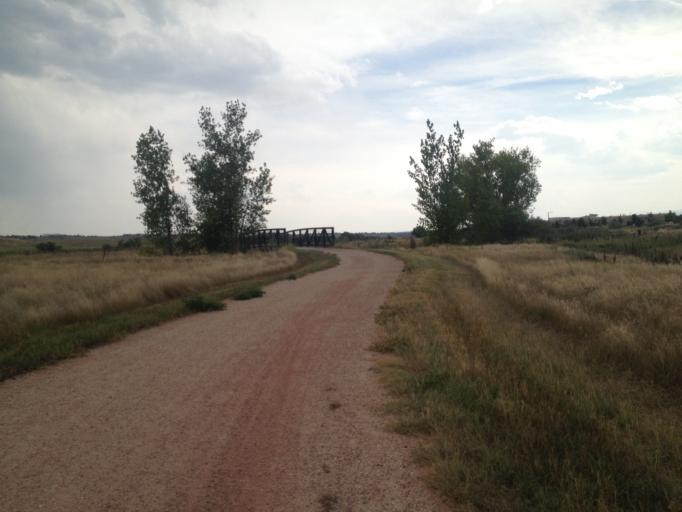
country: US
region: Colorado
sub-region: Boulder County
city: Lafayette
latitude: 39.9726
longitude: -105.0803
